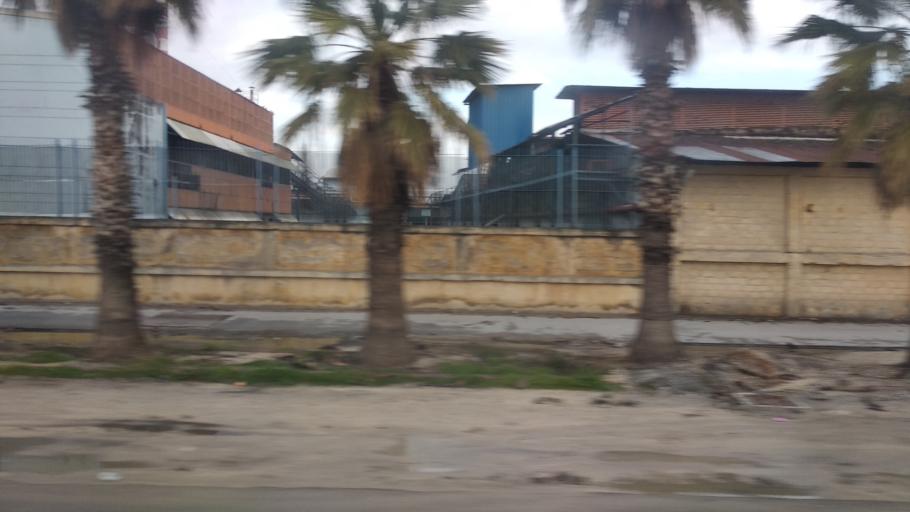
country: TR
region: Adana
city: Seyhan
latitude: 36.9949
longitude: 35.2125
